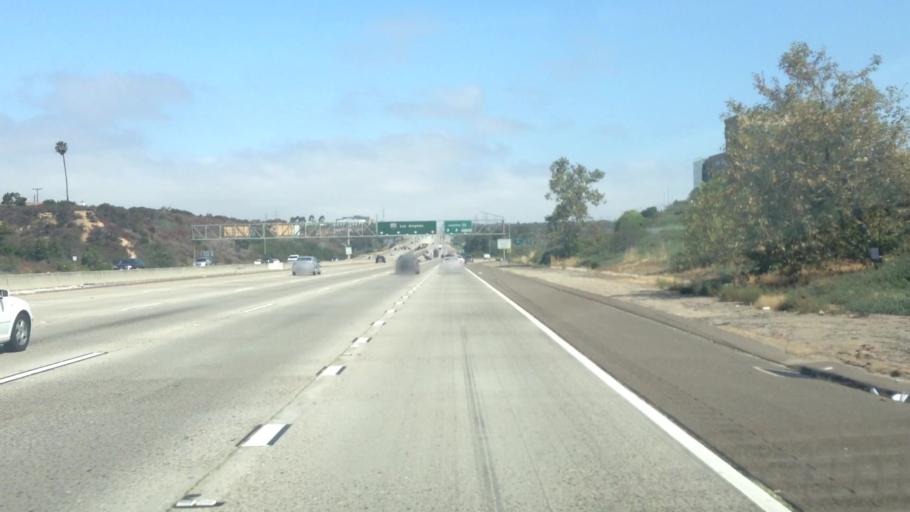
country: US
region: California
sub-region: San Diego County
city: La Jolla
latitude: 32.8404
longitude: -117.1735
